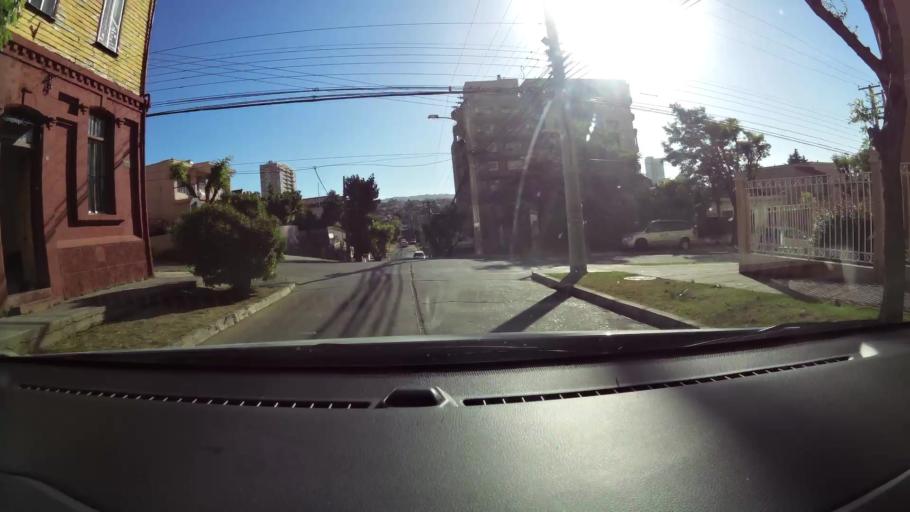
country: CL
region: Valparaiso
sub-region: Provincia de Valparaiso
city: Vina del Mar
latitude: -33.0284
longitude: -71.5716
